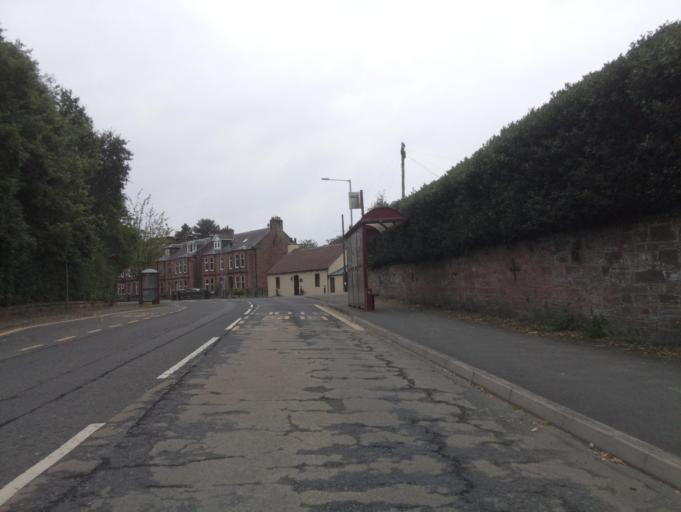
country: GB
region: Scotland
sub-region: Dumfries and Galloway
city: Dumfries
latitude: 55.0755
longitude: -3.5988
